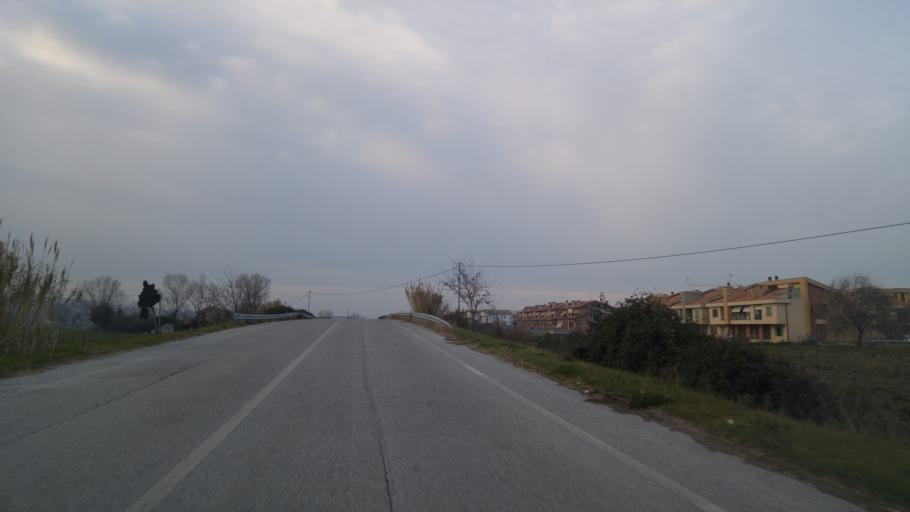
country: IT
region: The Marches
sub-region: Provincia di Pesaro e Urbino
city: Marotta
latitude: 43.7611
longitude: 13.1418
